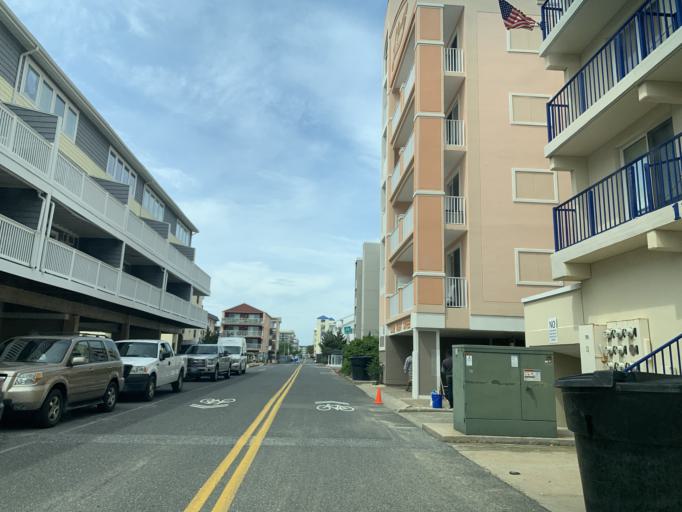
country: US
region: Delaware
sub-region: Sussex County
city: Bethany Beach
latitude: 38.4443
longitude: -75.0510
